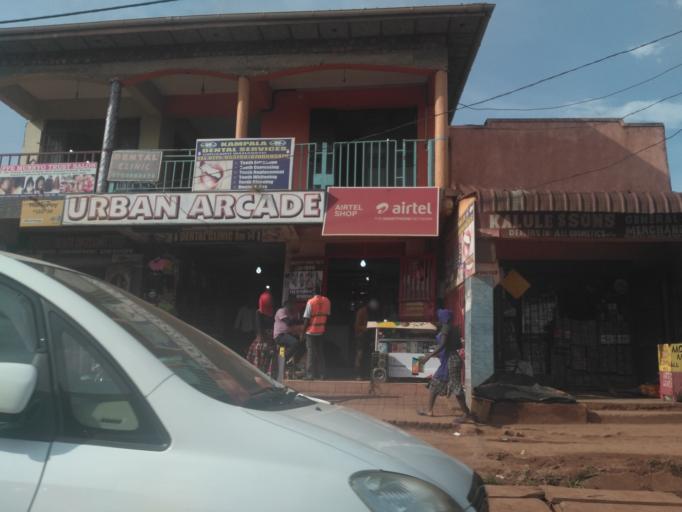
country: UG
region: Central Region
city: Kampala Central Division
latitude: 0.3527
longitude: 32.5614
